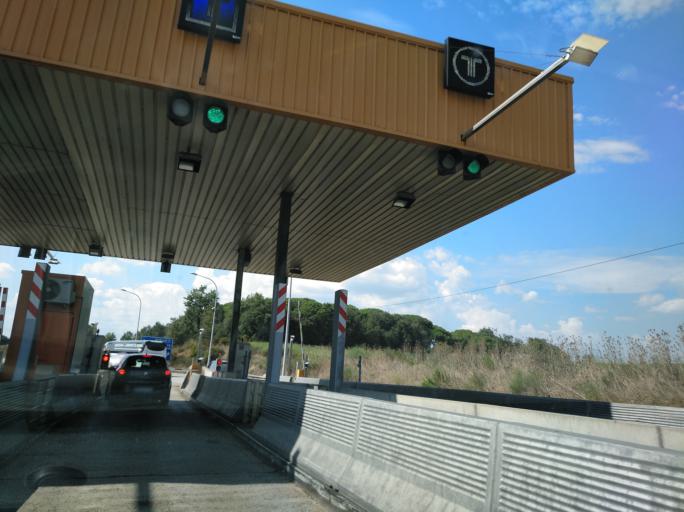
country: ES
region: Catalonia
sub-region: Provincia de Girona
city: Riudellots de la Selva
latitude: 41.8955
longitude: 2.7777
